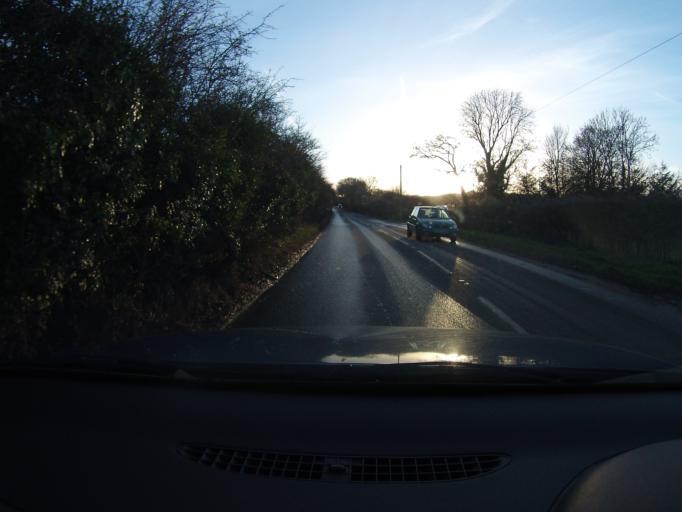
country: GB
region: England
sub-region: Isle of Wight
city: Ryde
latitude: 50.7128
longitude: -1.1610
